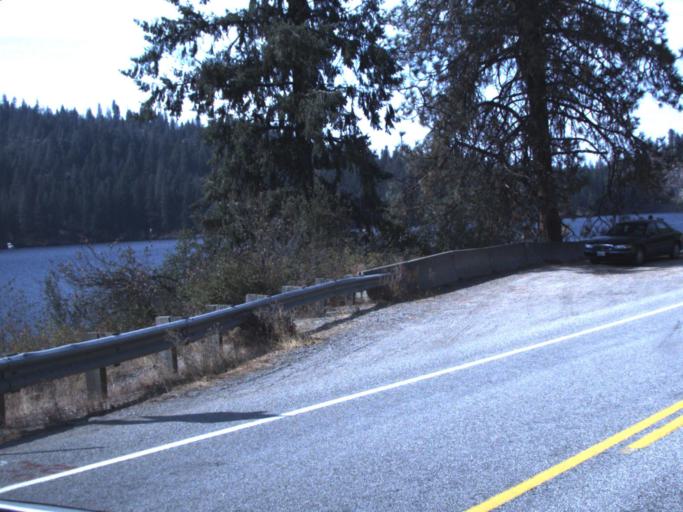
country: US
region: Washington
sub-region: Pend Oreille County
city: Newport
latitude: 48.2186
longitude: -117.2911
